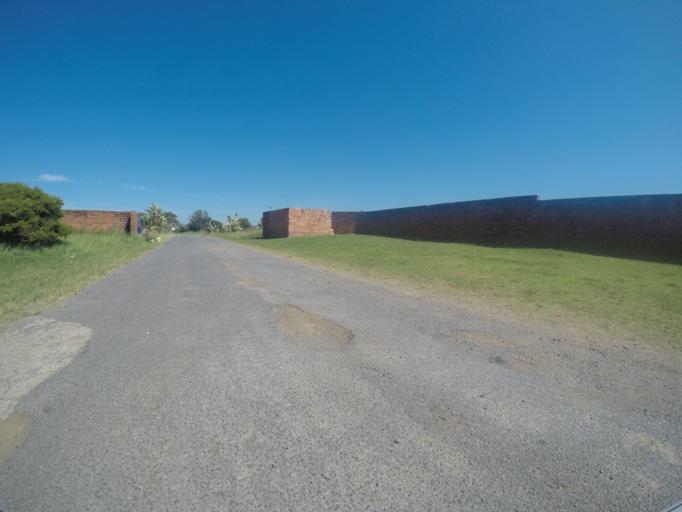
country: ZA
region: Eastern Cape
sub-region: Buffalo City Metropolitan Municipality
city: East London
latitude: -32.9511
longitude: 28.0063
